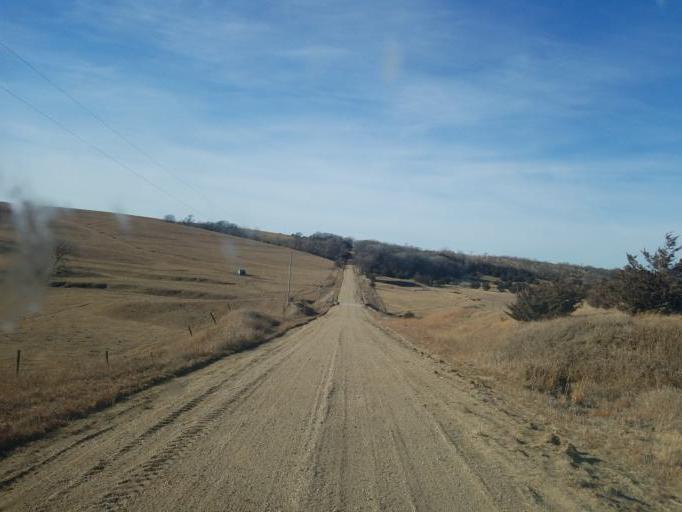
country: US
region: Nebraska
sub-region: Knox County
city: Center
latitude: 42.6554
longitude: -97.7912
